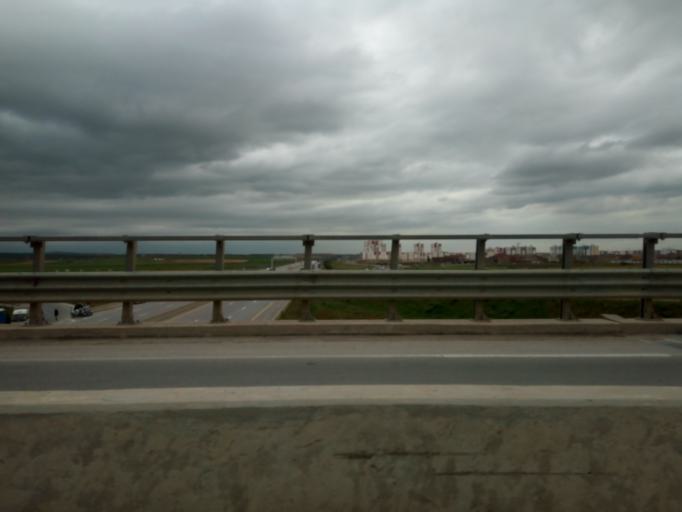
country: DZ
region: Setif
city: El Eulma
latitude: 36.1767
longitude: 5.6745
